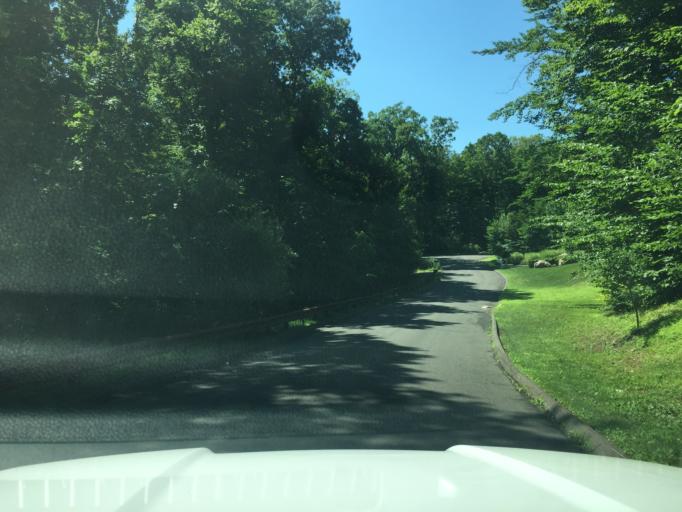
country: US
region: Connecticut
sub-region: Fairfield County
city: Westport
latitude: 41.2163
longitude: -73.3537
